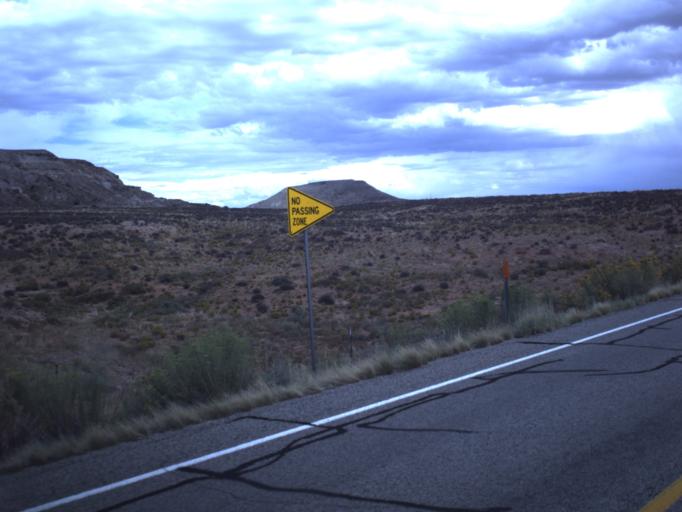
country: US
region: Utah
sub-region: San Juan County
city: Blanding
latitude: 37.3006
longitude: -109.4382
